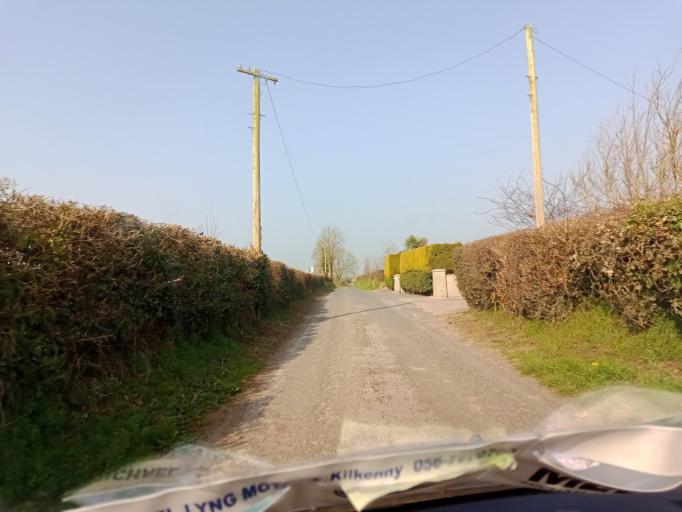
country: IE
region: Leinster
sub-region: Kilkenny
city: Callan
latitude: 52.5208
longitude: -7.4070
